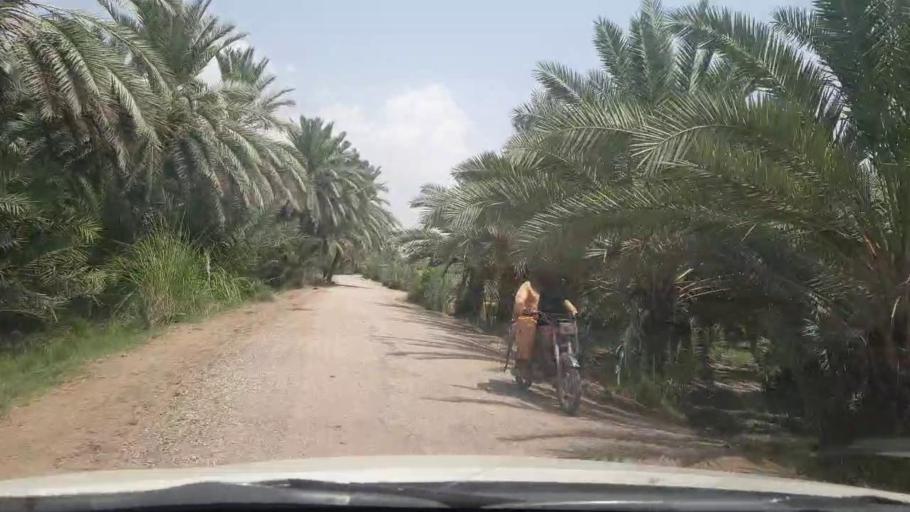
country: PK
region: Sindh
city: Khairpur
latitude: 27.5512
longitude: 68.8293
